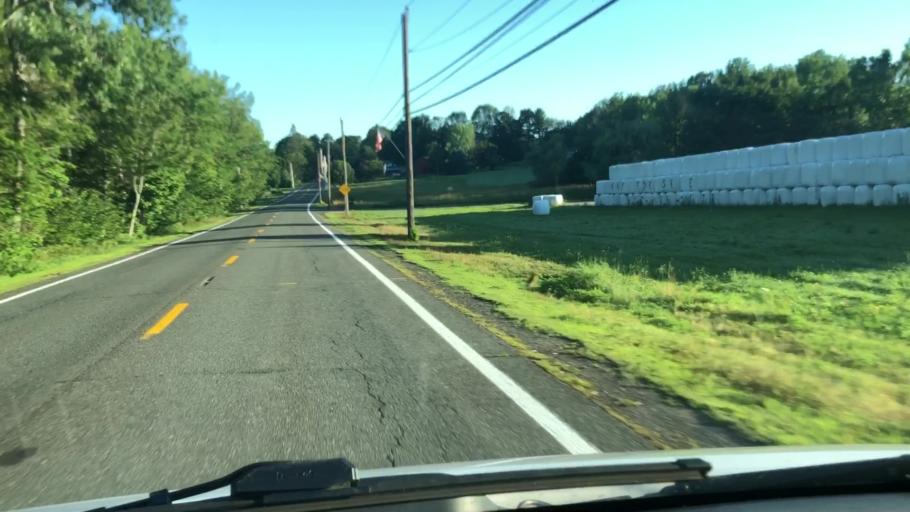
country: US
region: Massachusetts
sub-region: Hampshire County
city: Chesterfield
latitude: 42.3920
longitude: -72.9333
